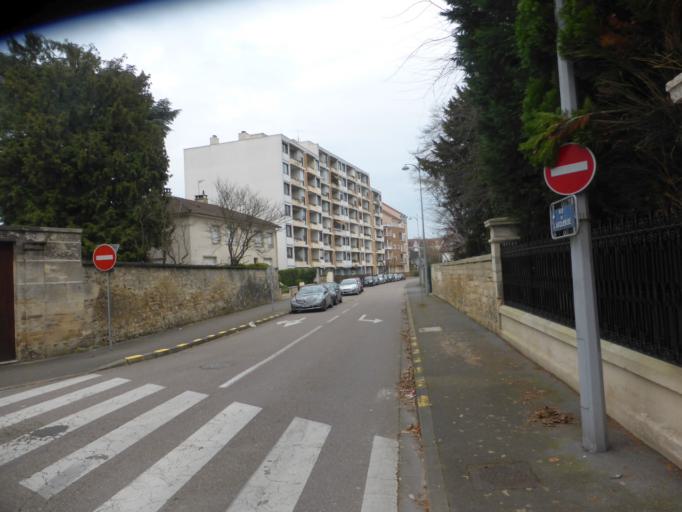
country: FR
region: Champagne-Ardenne
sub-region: Departement de la Haute-Marne
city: Saint-Dizier
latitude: 48.6359
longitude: 4.9423
